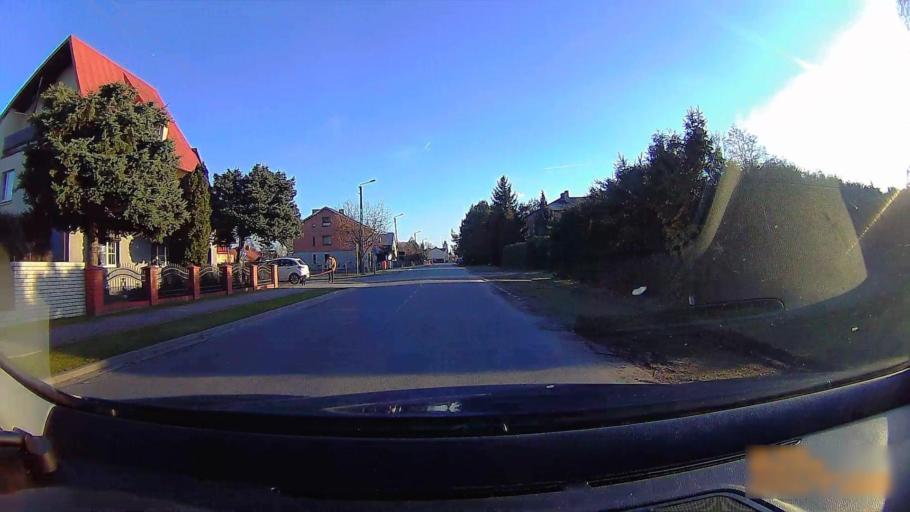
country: PL
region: Greater Poland Voivodeship
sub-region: Powiat koninski
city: Rychwal
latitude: 52.0735
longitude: 18.1665
